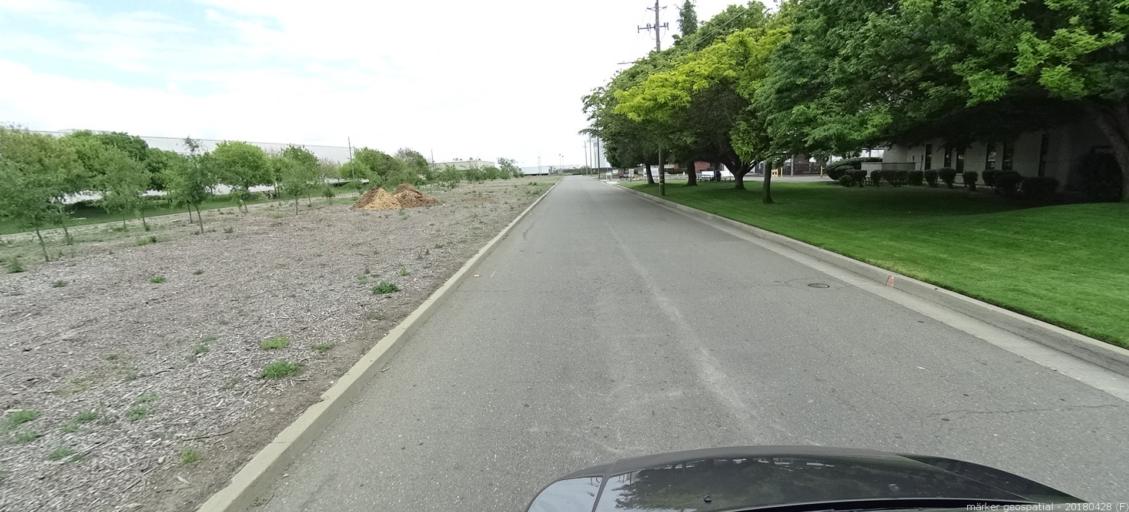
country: US
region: California
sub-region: Yolo County
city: West Sacramento
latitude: 38.5612
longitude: -121.5768
